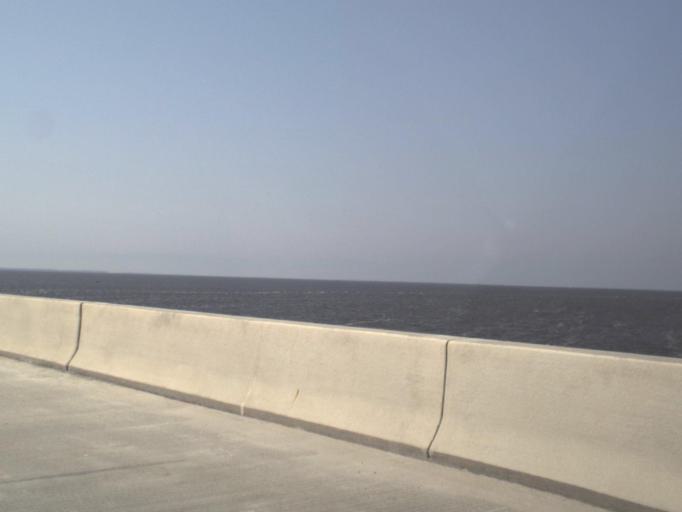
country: US
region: Florida
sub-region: Franklin County
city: Eastpoint
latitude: 29.7144
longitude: -84.8908
